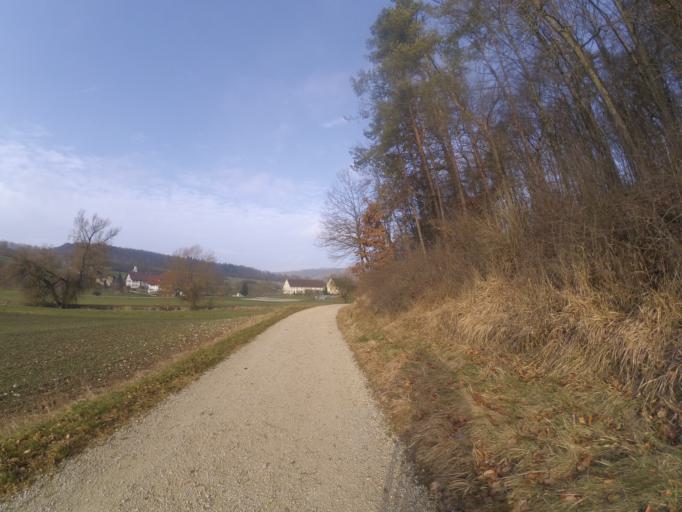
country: DE
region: Baden-Wuerttemberg
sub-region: Tuebingen Region
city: Rechtenstein
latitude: 48.2640
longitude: 9.5418
